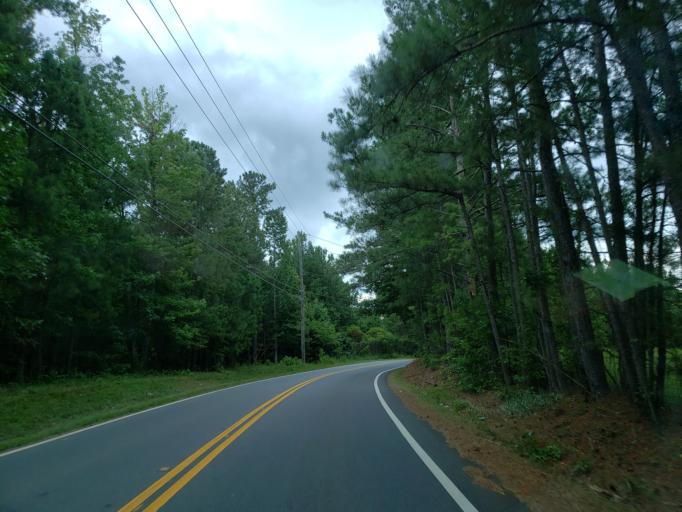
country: US
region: Georgia
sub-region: Paulding County
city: Dallas
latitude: 33.9984
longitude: -84.8026
